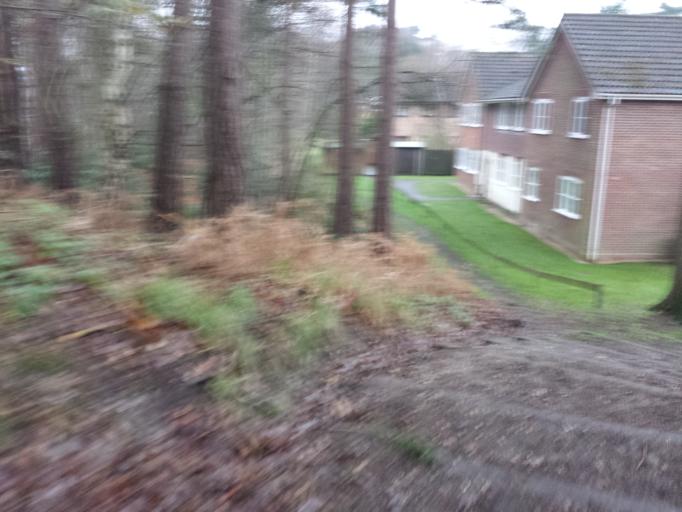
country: GB
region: England
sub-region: Surrey
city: Bagshot
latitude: 51.3521
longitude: -0.6914
